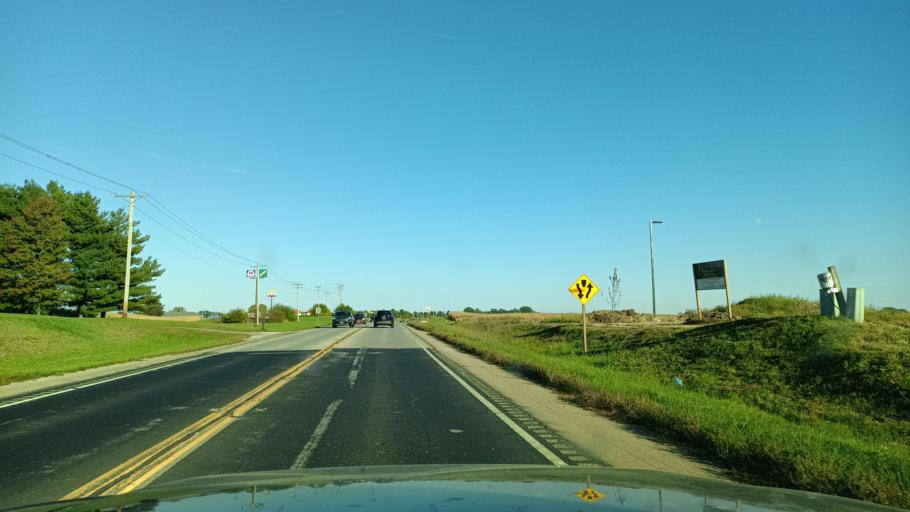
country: US
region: Illinois
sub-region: Champaign County
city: Lake of the Woods
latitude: 40.1858
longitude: -88.3739
